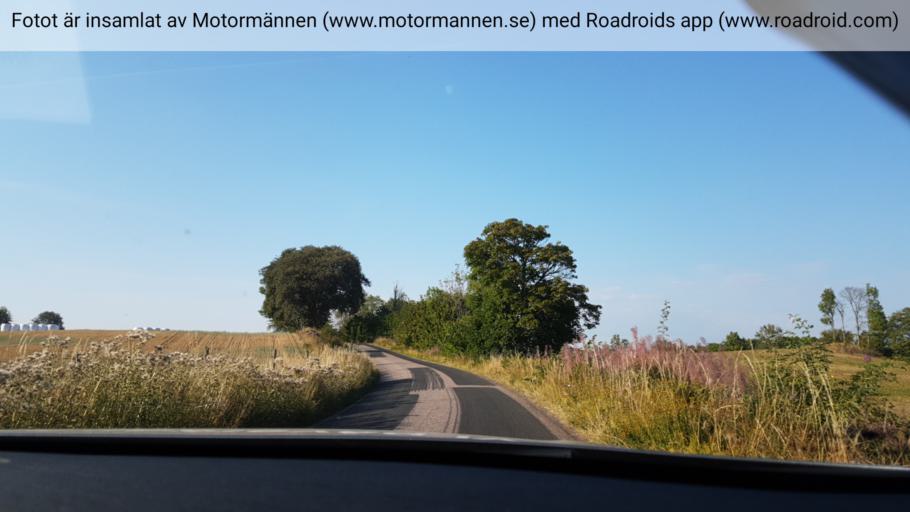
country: SE
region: Vaestra Goetaland
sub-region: Skovde Kommun
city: Stopen
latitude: 58.4678
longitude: 13.7442
